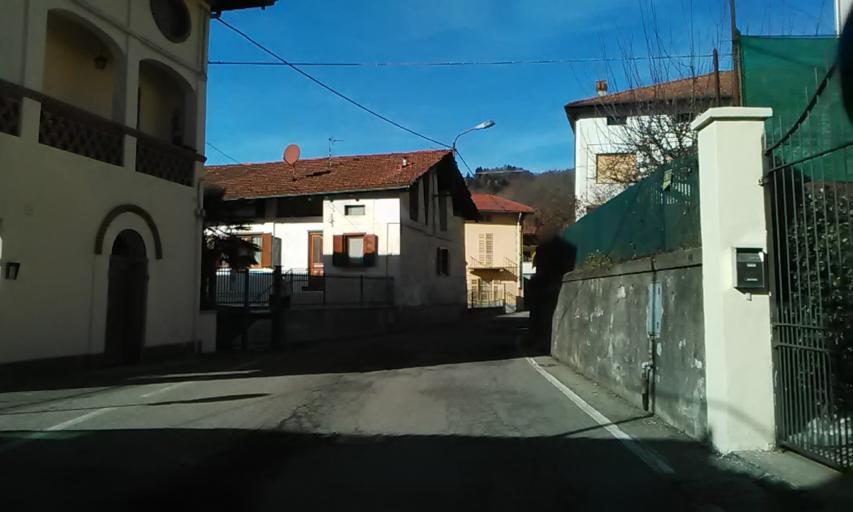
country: IT
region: Piedmont
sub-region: Provincia di Vercelli
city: Borgosesia
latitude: 45.7300
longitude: 8.2995
